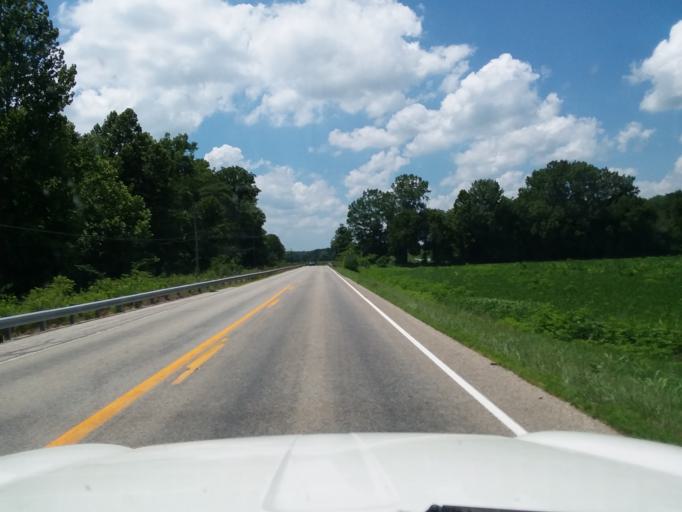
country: US
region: Indiana
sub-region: Johnson County
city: Trafalgar
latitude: 39.3712
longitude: -86.2824
